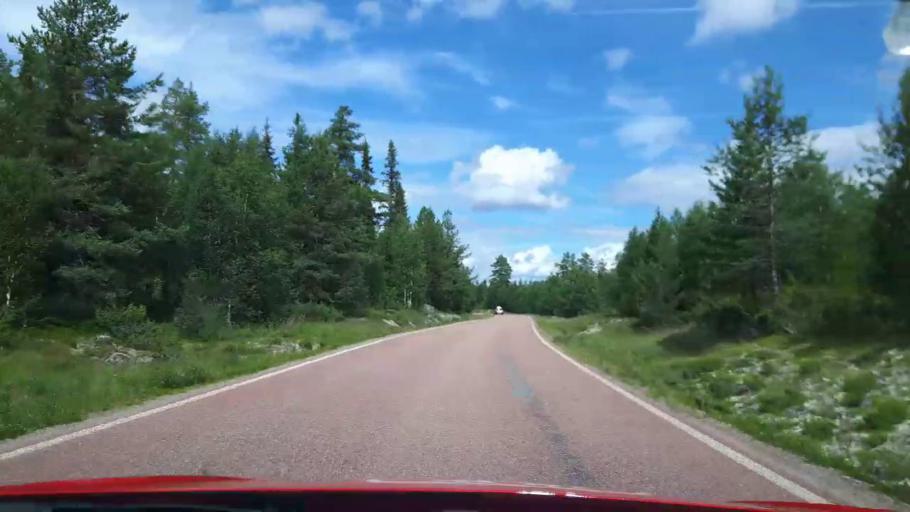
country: NO
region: Hedmark
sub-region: Trysil
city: Innbygda
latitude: 62.0170
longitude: 12.9785
